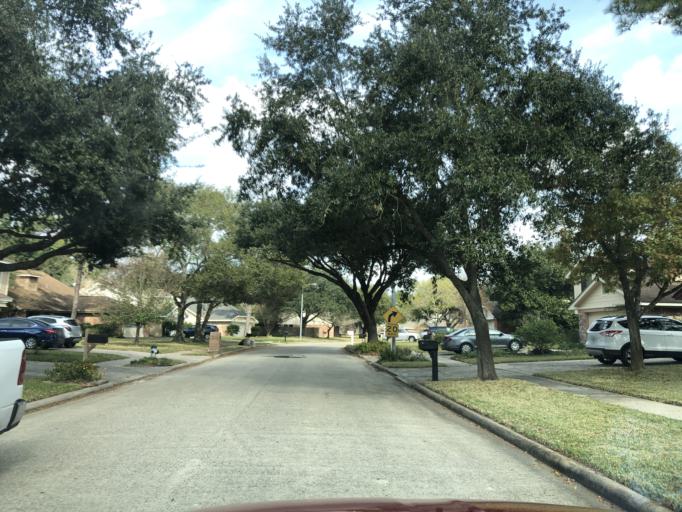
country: US
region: Texas
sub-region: Harris County
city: Tomball
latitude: 30.0365
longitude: -95.5417
